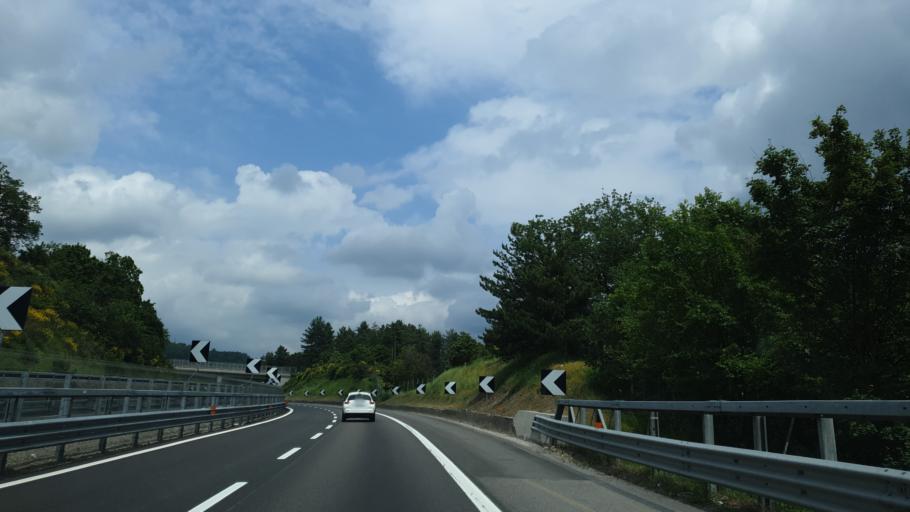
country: IT
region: Tuscany
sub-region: Province of Florence
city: Barberino di Mugello
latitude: 44.0037
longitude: 11.2193
